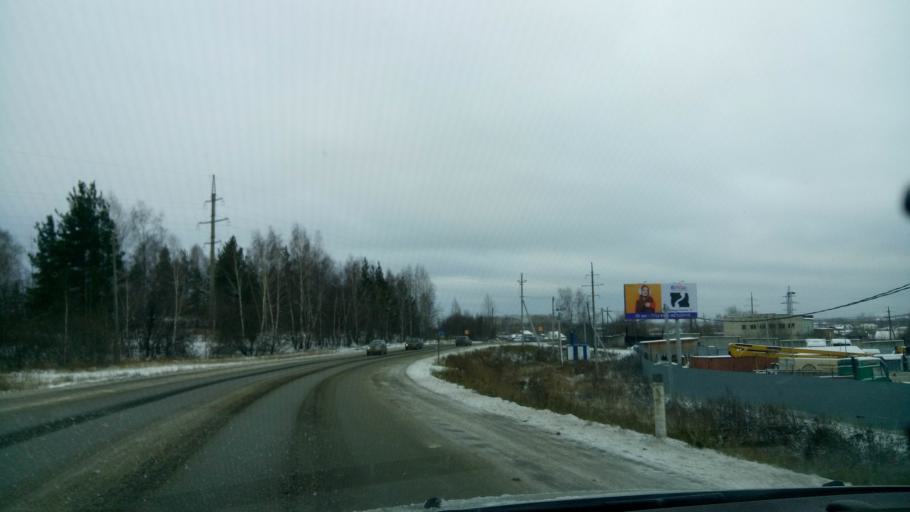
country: RU
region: Sverdlovsk
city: Polevskoy
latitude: 56.4592
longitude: 60.2133
